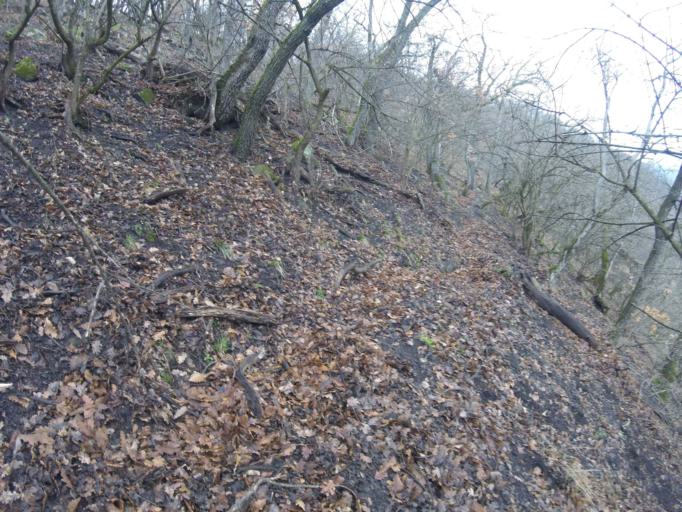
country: HU
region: Pest
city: Visegrad
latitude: 47.7590
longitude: 18.9861
